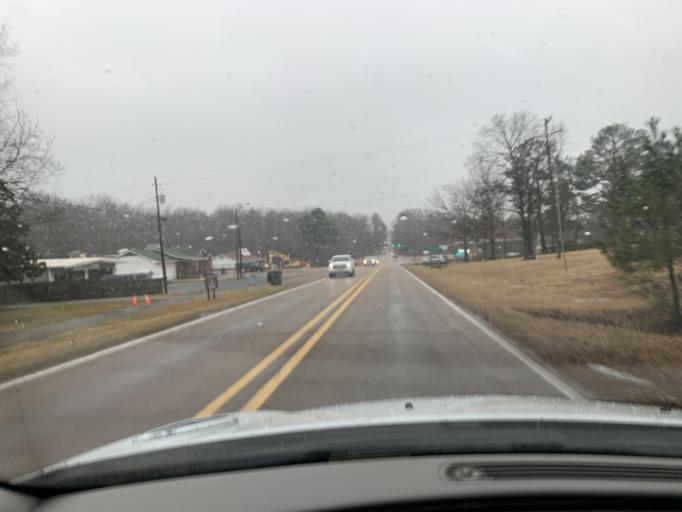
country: US
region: Mississippi
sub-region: De Soto County
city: Hernando
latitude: 34.8855
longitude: -89.9963
